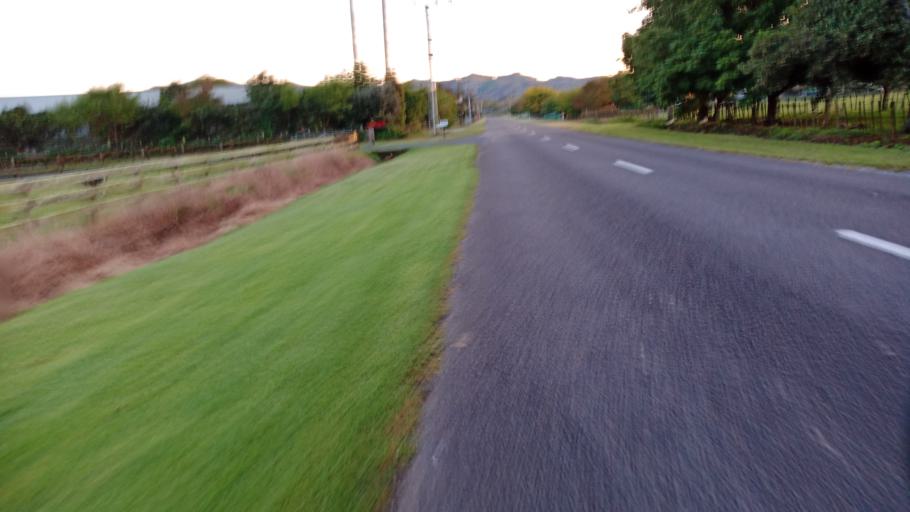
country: NZ
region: Gisborne
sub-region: Gisborne District
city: Gisborne
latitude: -38.6374
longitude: 177.9850
